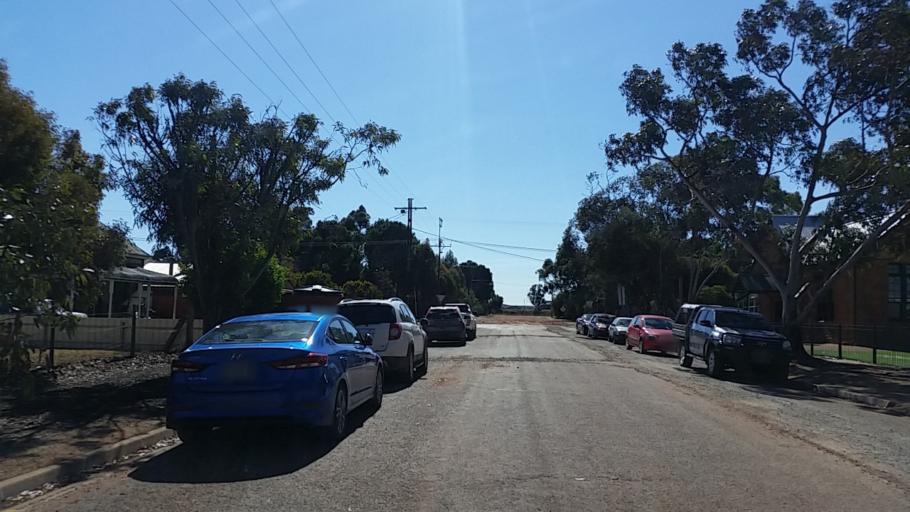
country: AU
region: South Australia
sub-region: Peterborough
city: Peterborough
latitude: -32.9753
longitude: 138.8415
